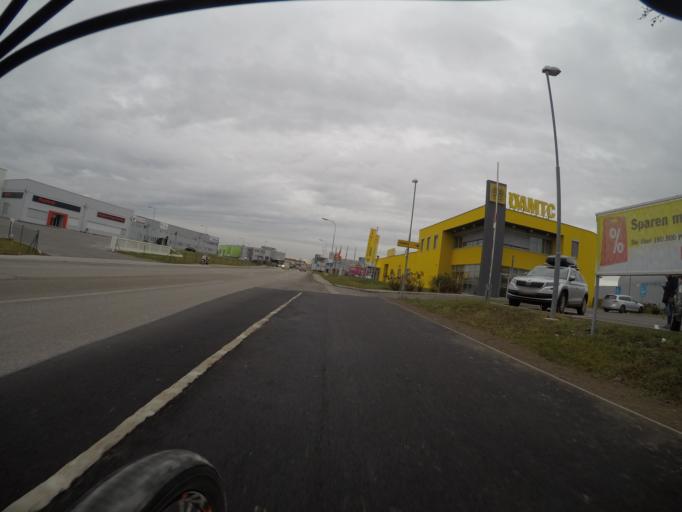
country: AT
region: Lower Austria
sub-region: Politischer Bezirk Modling
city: Wiener Neudorf
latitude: 48.1076
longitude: 16.3104
